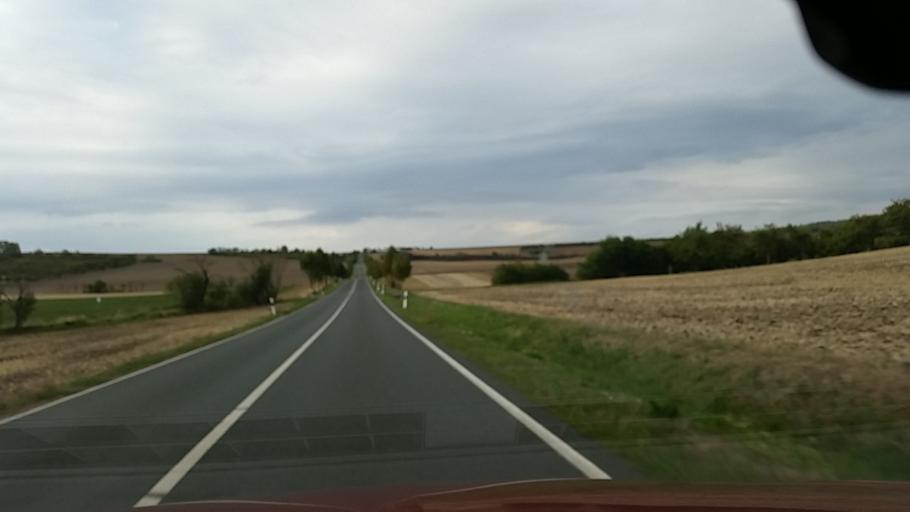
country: DE
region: Thuringia
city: Beichlingen
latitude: 51.2099
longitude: 11.2578
